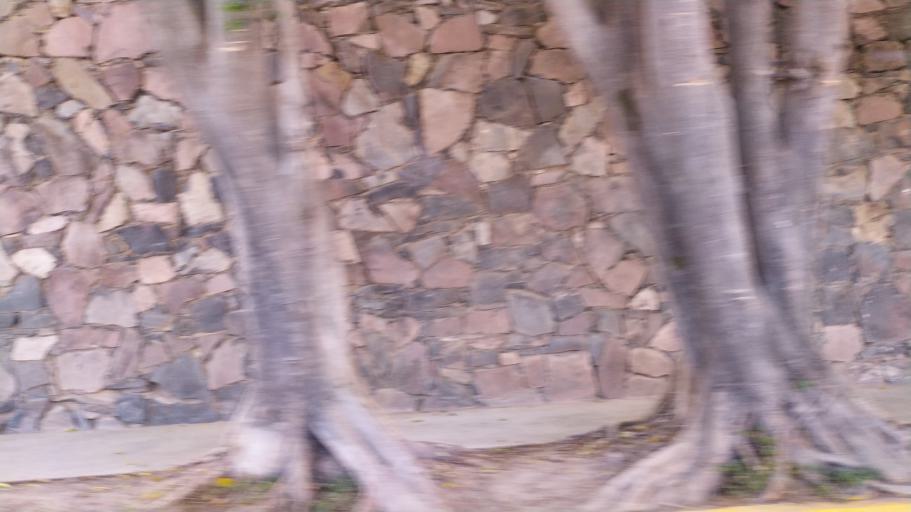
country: MX
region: Jalisco
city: Guadalajara
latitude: 20.6766
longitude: -103.4009
